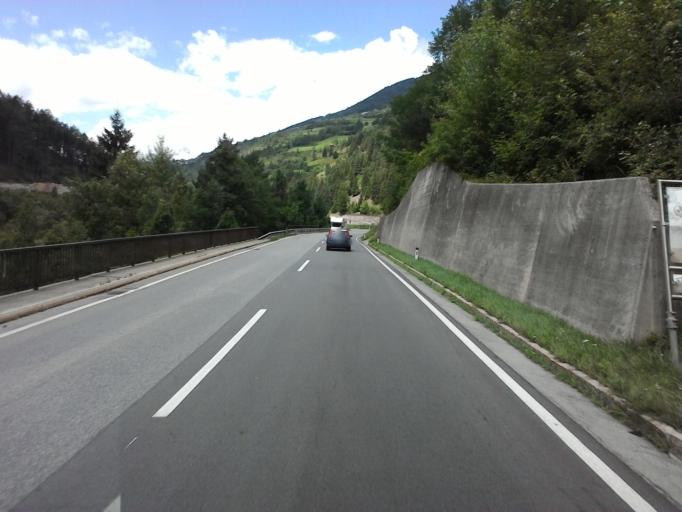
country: AT
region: Tyrol
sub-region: Politischer Bezirk Landeck
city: Prutz
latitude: 47.1113
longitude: 10.6577
